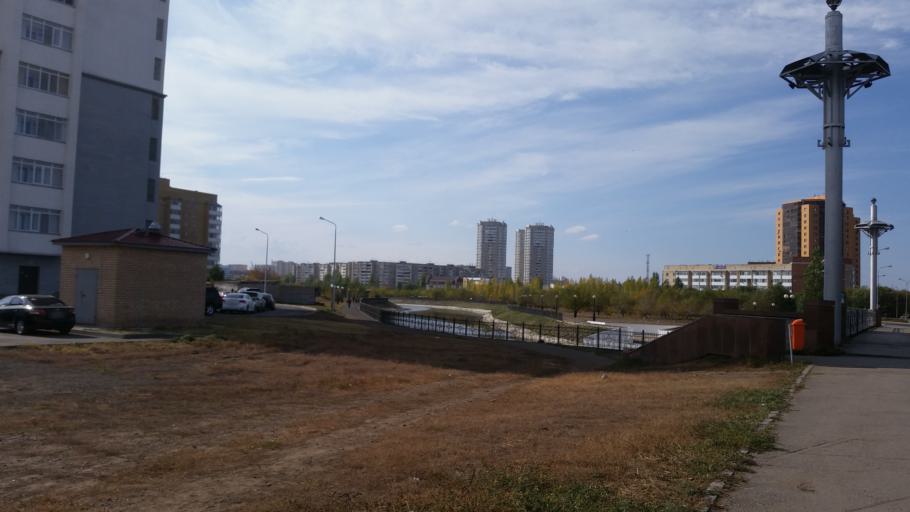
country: KZ
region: Astana Qalasy
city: Astana
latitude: 51.1641
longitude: 71.4784
